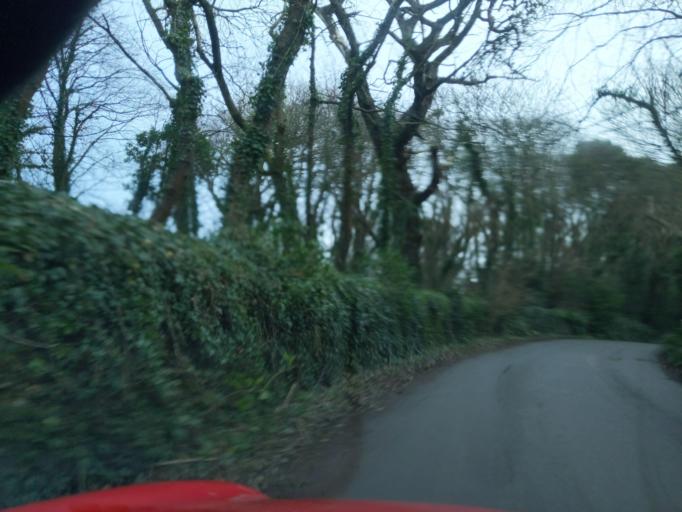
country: GB
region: England
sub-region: Devon
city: Wembury
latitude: 50.3282
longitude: -4.0893
